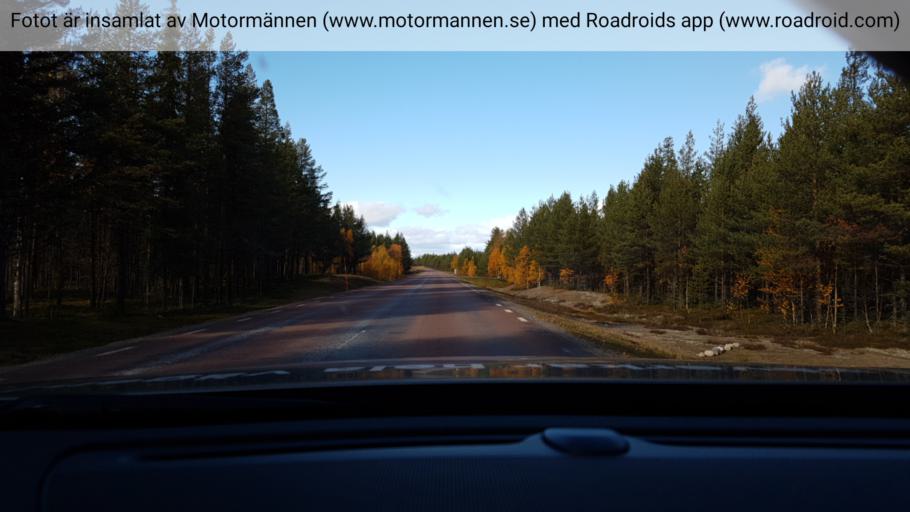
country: SE
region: Norrbotten
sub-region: Arjeplogs Kommun
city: Arjeplog
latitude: 65.9954
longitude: 18.1676
